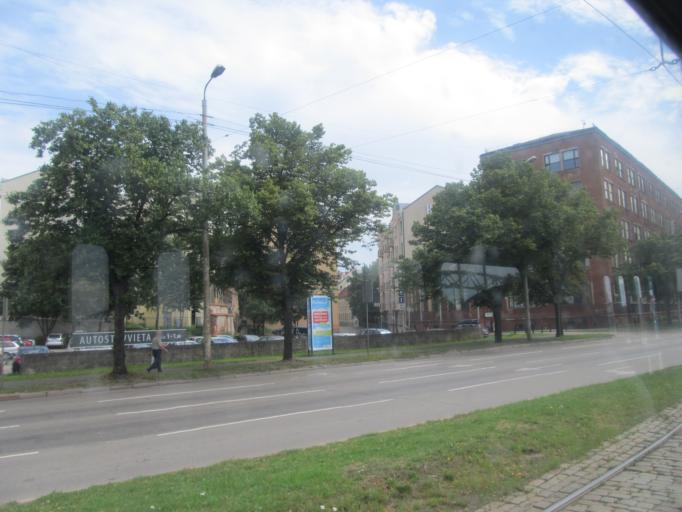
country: LV
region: Riga
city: Riga
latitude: 56.9452
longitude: 24.1069
